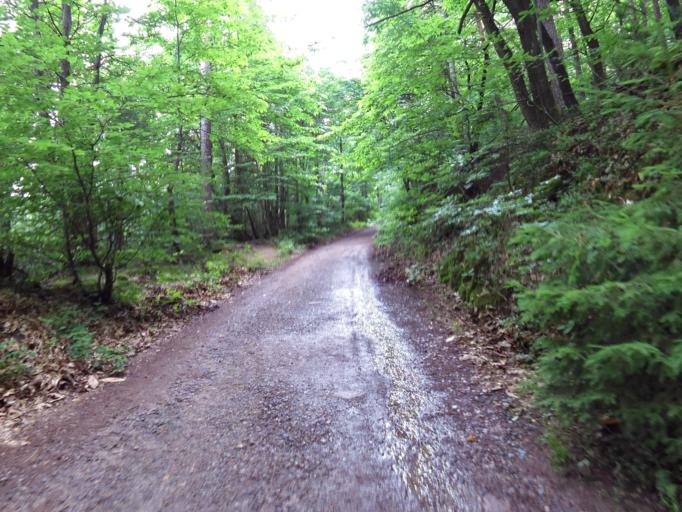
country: DE
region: Rheinland-Pfalz
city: Weisenheim am Berg
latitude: 49.5009
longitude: 8.1240
